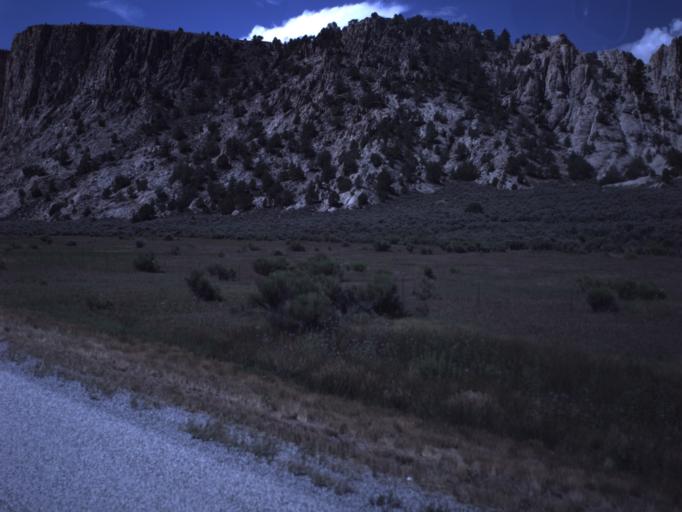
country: US
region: Utah
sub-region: Garfield County
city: Panguitch
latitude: 38.0339
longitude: -112.3566
